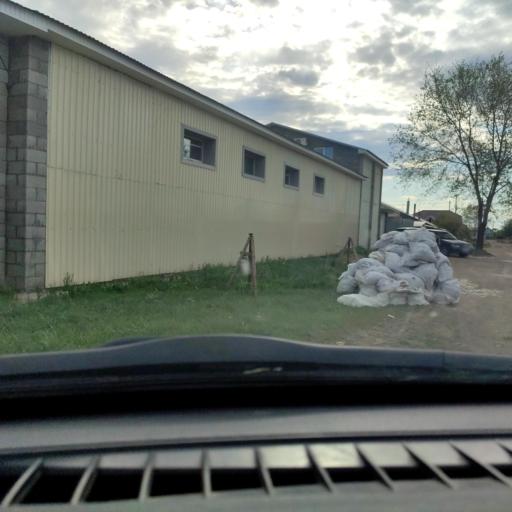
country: RU
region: Samara
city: Tol'yatti
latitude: 53.5748
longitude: 49.4138
